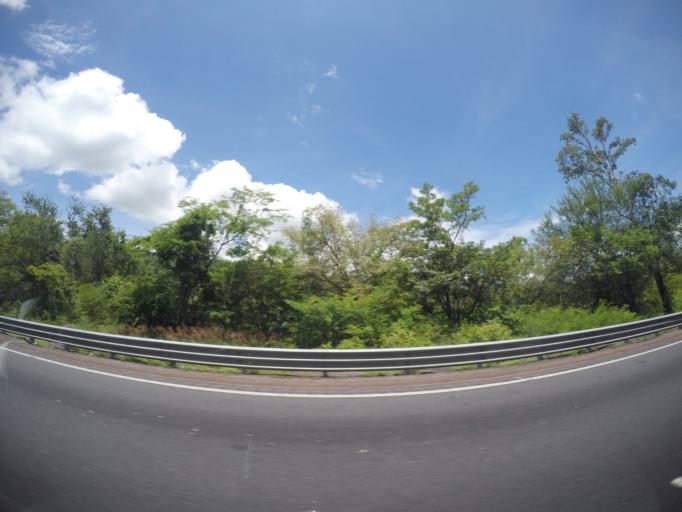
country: MX
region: Morelos
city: Tilzapotla
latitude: 18.4079
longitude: -99.1725
